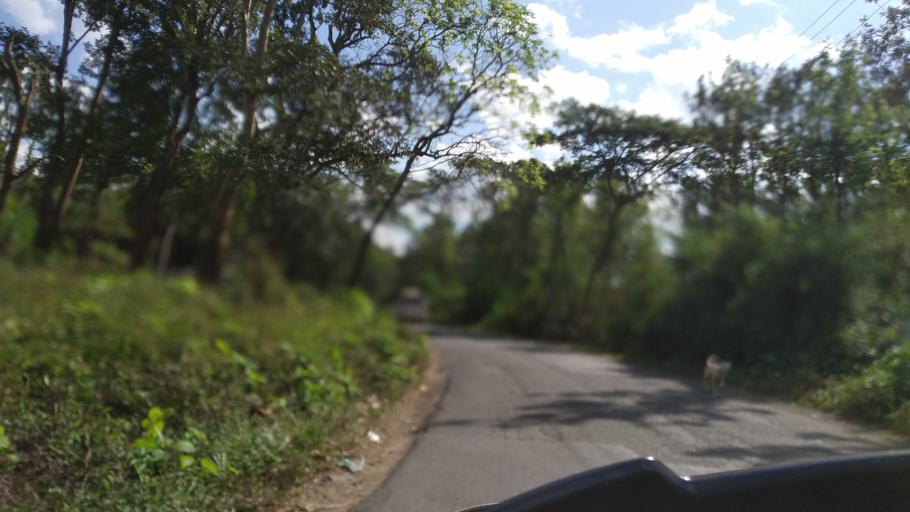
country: IN
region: Kerala
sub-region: Wayanad
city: Panamaram
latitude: 11.9481
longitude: 76.0640
